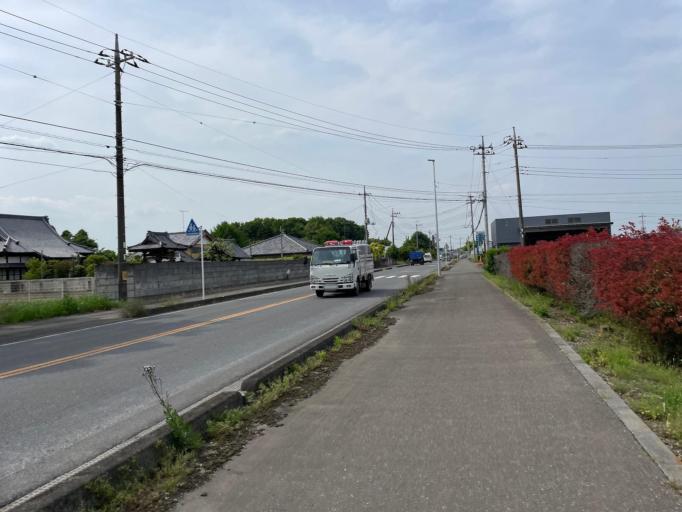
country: JP
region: Tochigi
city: Mibu
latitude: 36.3850
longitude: 139.8046
